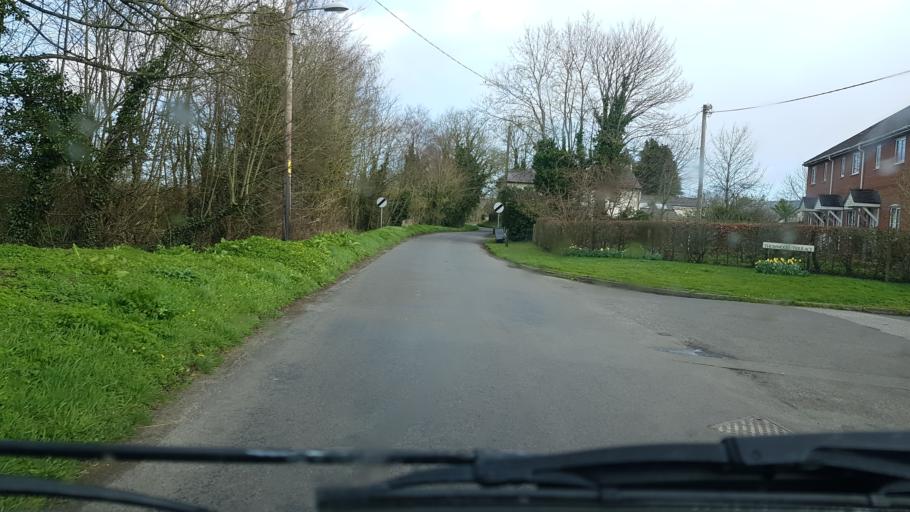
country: GB
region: England
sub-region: Wiltshire
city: Wilsford
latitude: 51.3142
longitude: -1.8932
